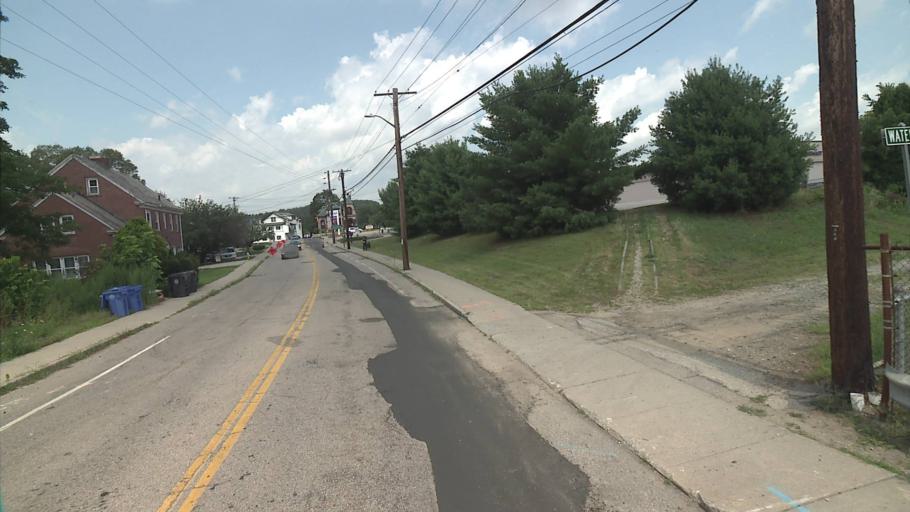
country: US
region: Connecticut
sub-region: New London County
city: Jewett City
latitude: 41.6038
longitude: -71.9831
